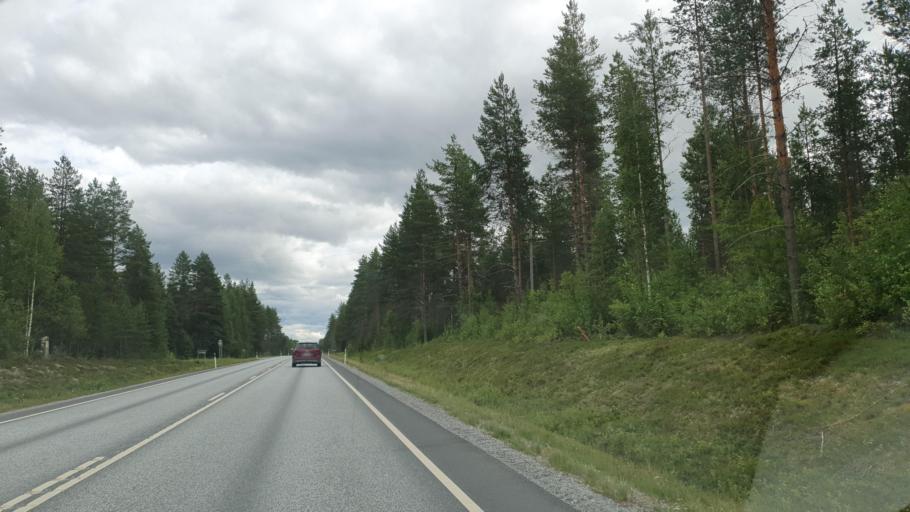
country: FI
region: Northern Savo
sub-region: Ylae-Savo
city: Sonkajaervi
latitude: 63.8958
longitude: 27.4088
